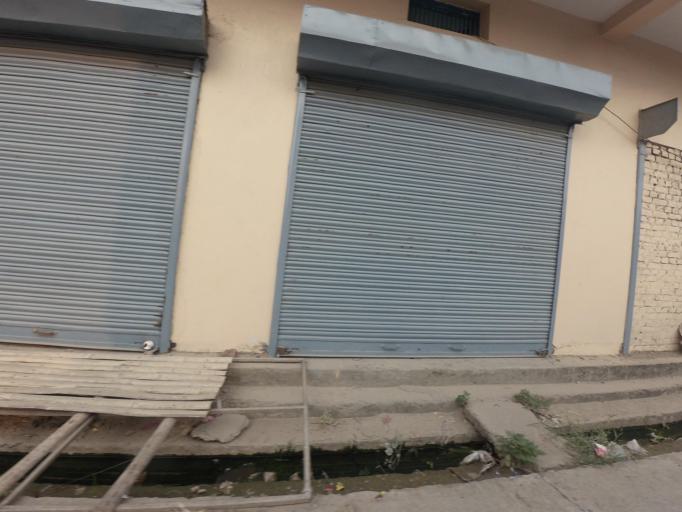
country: NP
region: Western Region
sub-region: Lumbini Zone
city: Bhairahawa
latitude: 27.5079
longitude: 83.4416
